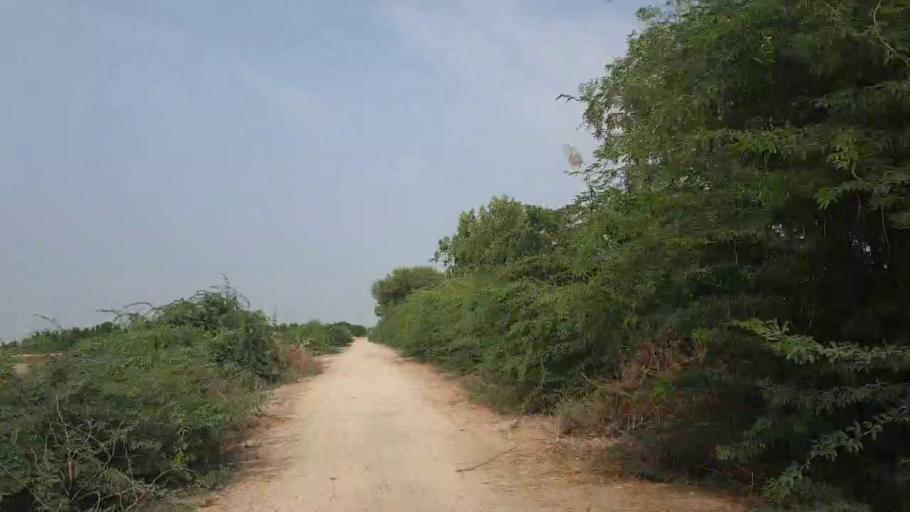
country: PK
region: Sindh
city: Badin
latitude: 24.6010
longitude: 68.7413
